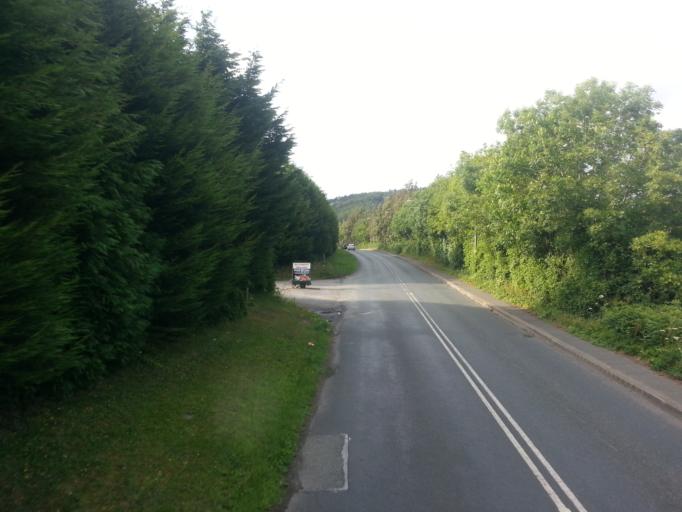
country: IE
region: Leinster
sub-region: Wicklow
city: Enniskerry
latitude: 53.2080
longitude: -6.1742
